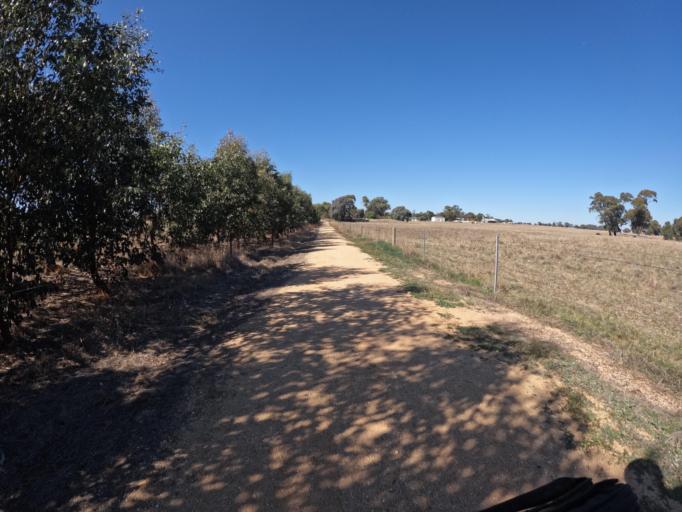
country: AU
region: Victoria
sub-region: Greater Bendigo
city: Kennington
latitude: -36.8243
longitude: 144.5821
